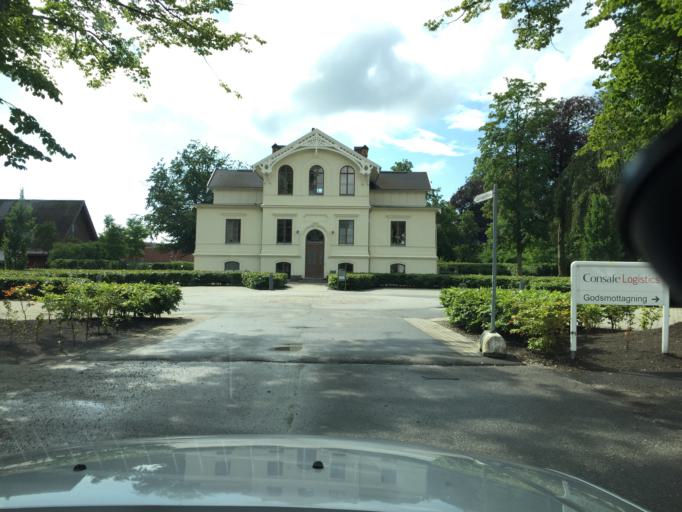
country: SE
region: Skane
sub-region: Lunds Kommun
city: Lund
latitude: 55.6894
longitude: 13.1967
